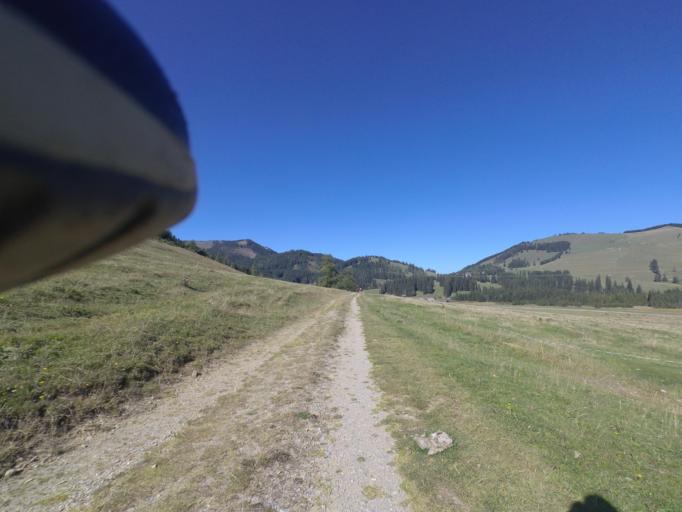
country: AT
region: Styria
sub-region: Politischer Bezirk Weiz
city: Passail
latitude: 47.3431
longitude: 15.4653
